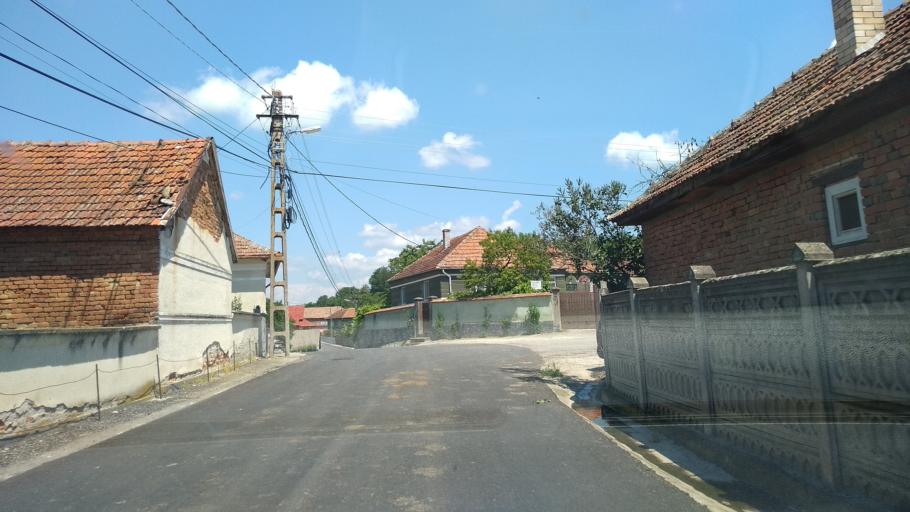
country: RO
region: Hunedoara
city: Berca
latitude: 45.6320
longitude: 23.0333
